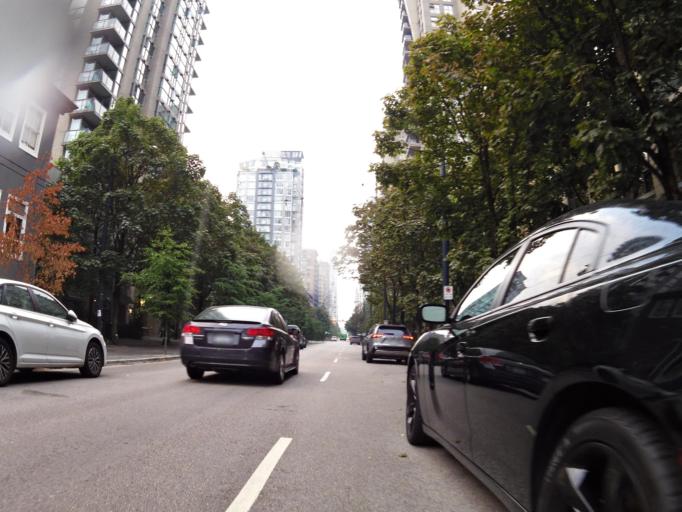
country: CA
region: British Columbia
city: West End
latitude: 49.2794
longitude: -123.1197
